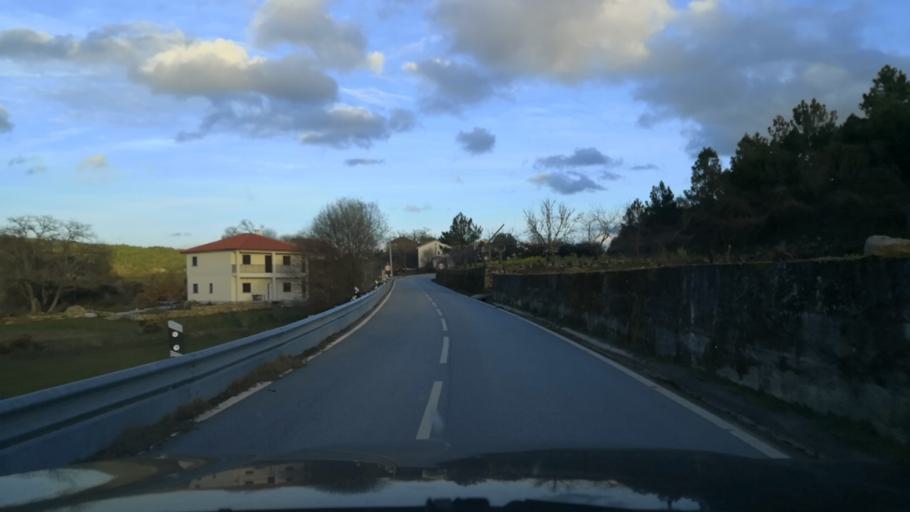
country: PT
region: Braganca
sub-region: Carrazeda de Ansiaes
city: Carrazeda de Anciaes
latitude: 41.2123
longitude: -7.3254
